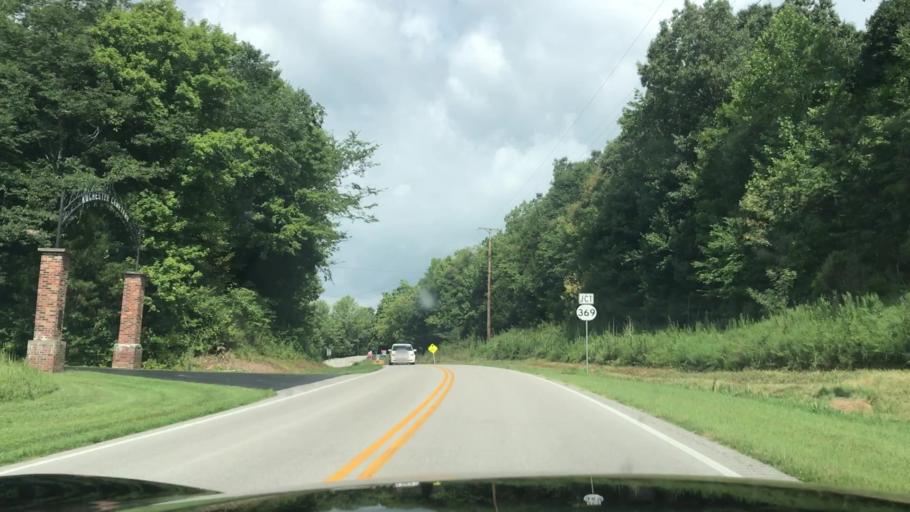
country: US
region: Kentucky
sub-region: Ohio County
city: Oak Grove
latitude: 37.2061
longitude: -86.8892
